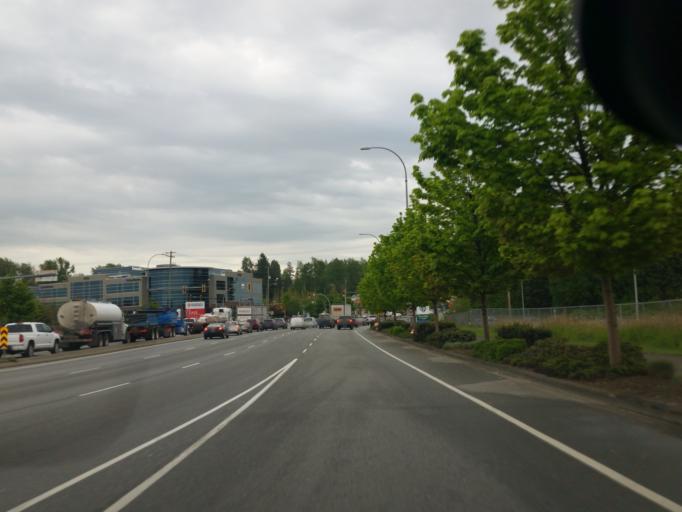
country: CA
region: British Columbia
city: Walnut Grove
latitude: 49.1624
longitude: -122.6691
